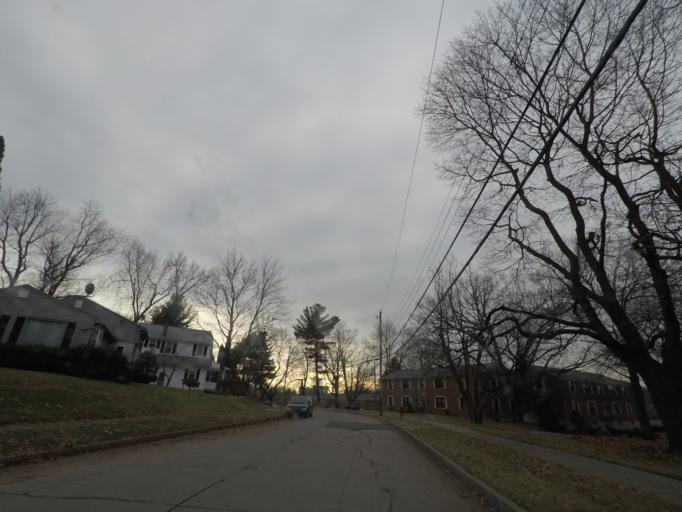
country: US
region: New York
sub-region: Albany County
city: Green Island
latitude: 42.7403
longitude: -73.6677
